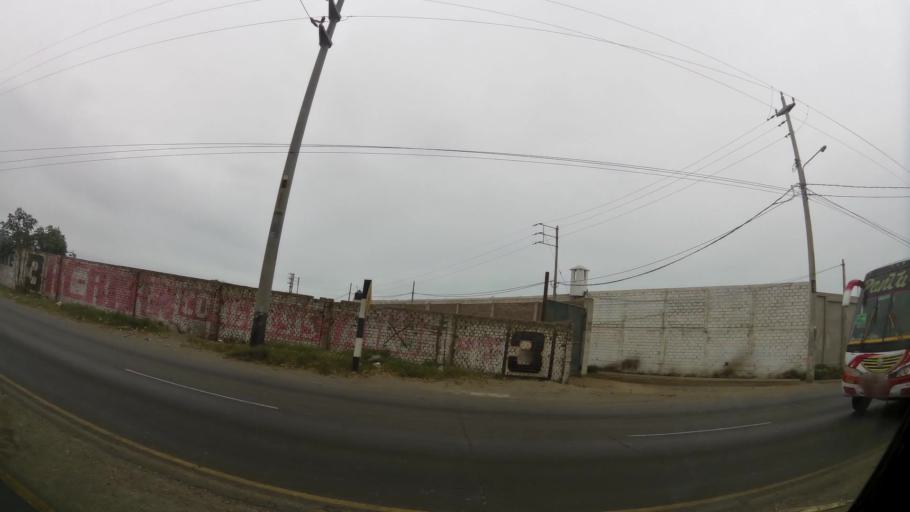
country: PE
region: La Libertad
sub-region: Provincia de Trujillo
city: Moche
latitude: -8.1733
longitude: -78.9991
